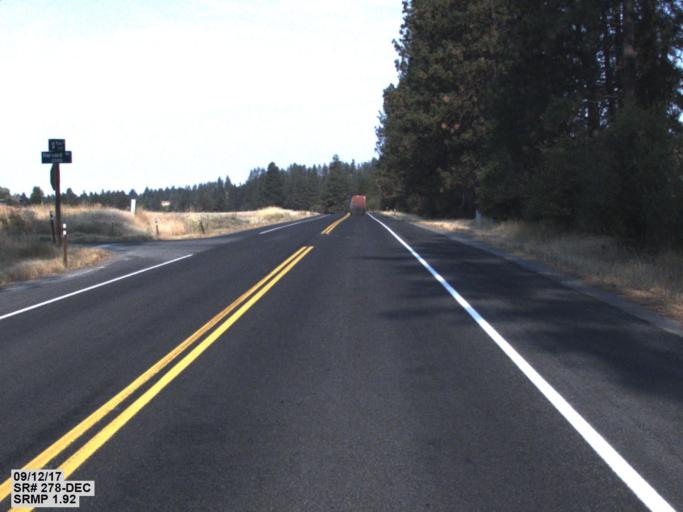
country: US
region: Washington
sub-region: Spokane County
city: Veradale
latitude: 47.4425
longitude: -117.1098
